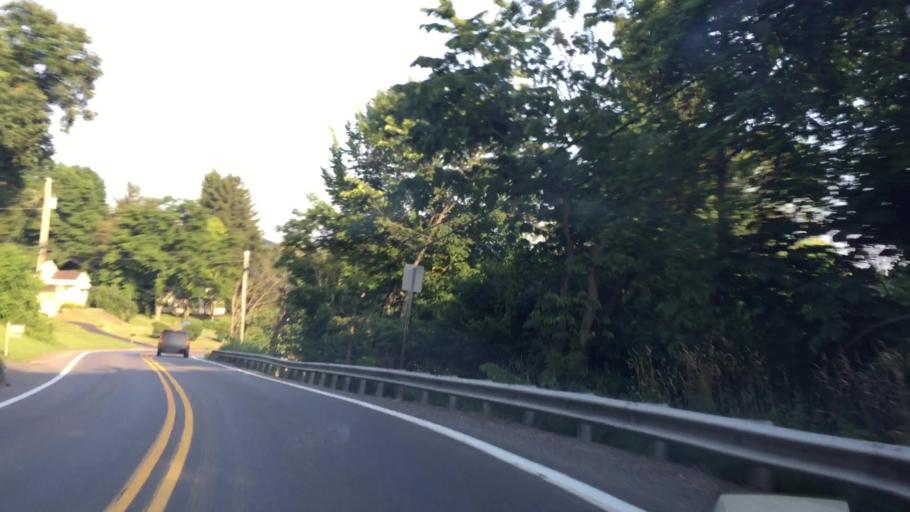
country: US
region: Pennsylvania
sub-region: Washington County
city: Thompsonville
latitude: 40.3213
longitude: -80.1217
